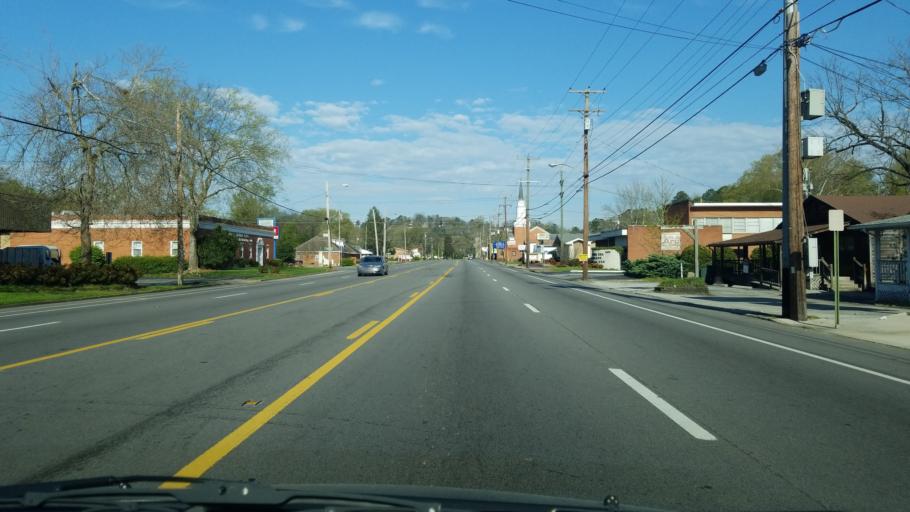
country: US
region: Tennessee
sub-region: Hamilton County
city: East Ridge
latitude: 35.0142
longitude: -85.2312
